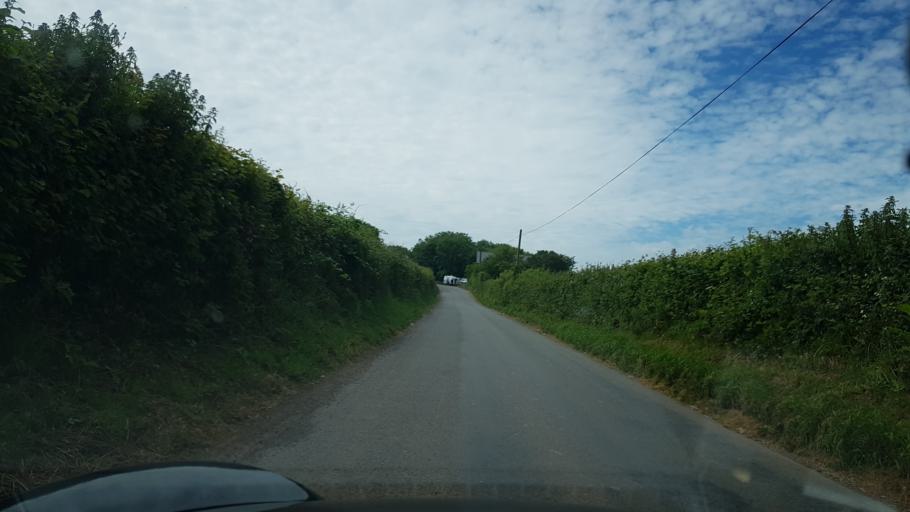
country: GB
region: Wales
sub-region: Carmarthenshire
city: Llanddowror
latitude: 51.7672
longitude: -4.5455
